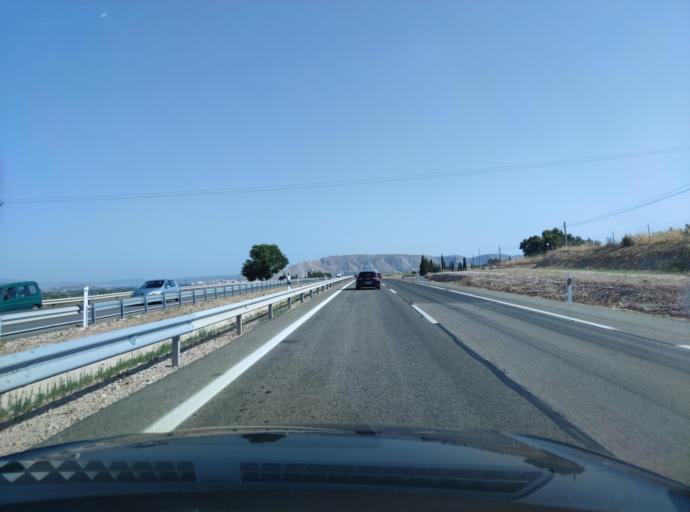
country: ES
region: Valencia
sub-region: Provincia de Alicante
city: Villena
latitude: 38.5885
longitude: -0.8438
